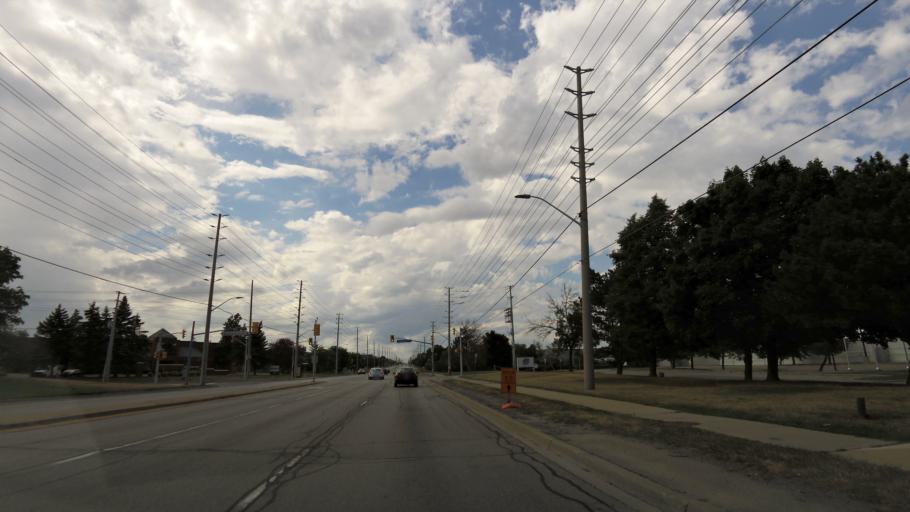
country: CA
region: Ontario
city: Mississauga
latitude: 43.6568
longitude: -79.6729
